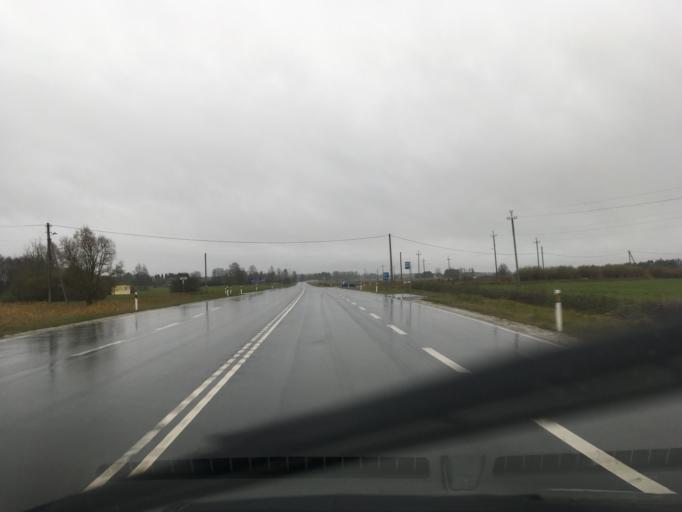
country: EE
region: Harju
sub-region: Nissi vald
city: Turba
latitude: 58.8842
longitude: 24.0892
